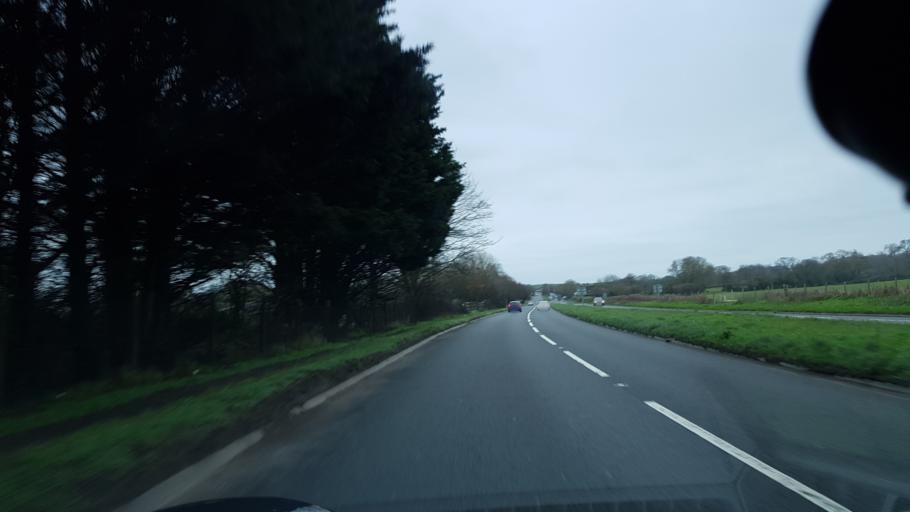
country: GB
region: England
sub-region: Somerset
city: Creech Saint Michael
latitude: 51.0100
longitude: -3.0365
